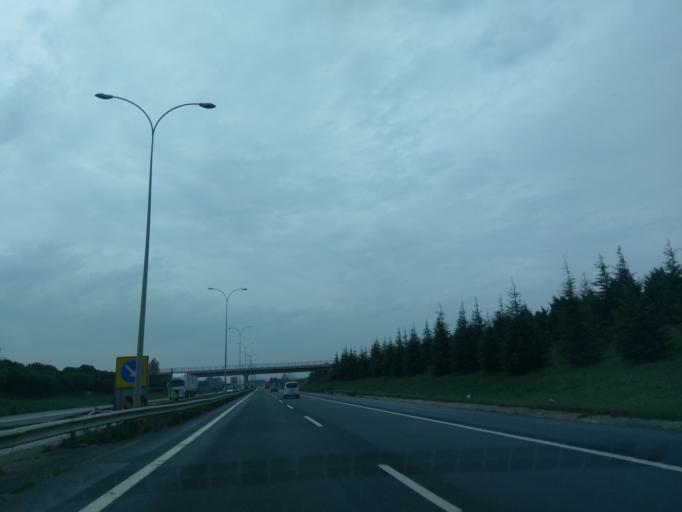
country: TR
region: Istanbul
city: Silivri
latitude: 41.1182
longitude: 28.2012
